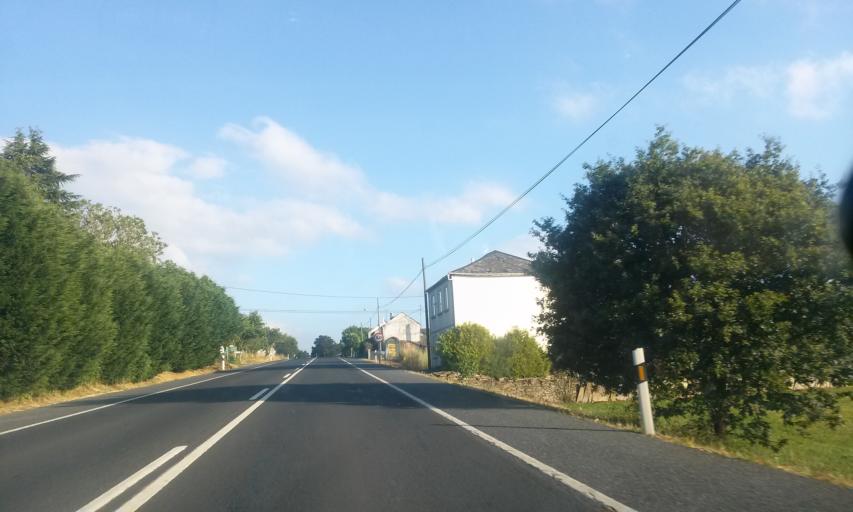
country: ES
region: Galicia
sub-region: Provincia de Lugo
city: Outeiro de Rei
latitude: 43.0758
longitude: -7.6048
